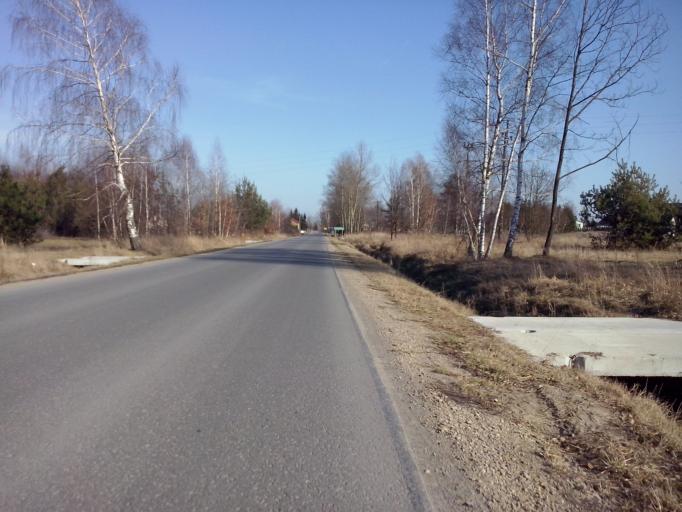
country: PL
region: Subcarpathian Voivodeship
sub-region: Powiat nizanski
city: Krzeszow
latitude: 50.4146
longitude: 22.3706
